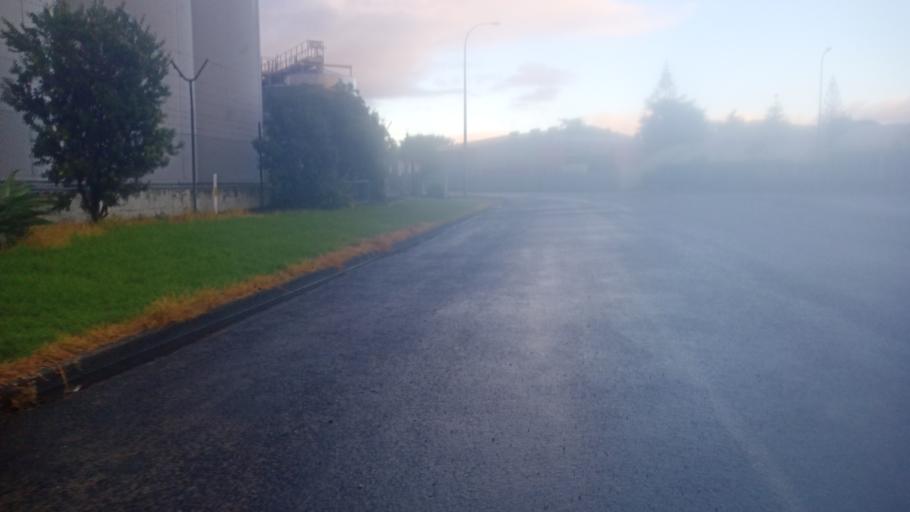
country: NZ
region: Gisborne
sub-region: Gisborne District
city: Gisborne
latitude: -38.6680
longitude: 177.9981
